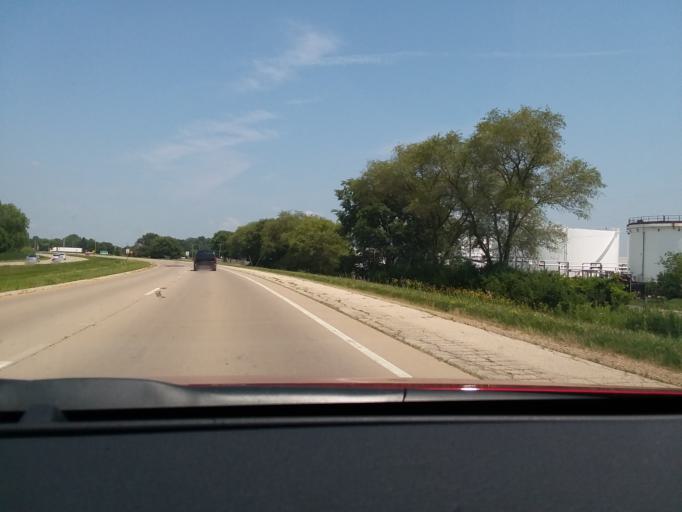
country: US
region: Wisconsin
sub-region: Dane County
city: McFarland
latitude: 43.0364
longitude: -89.2994
